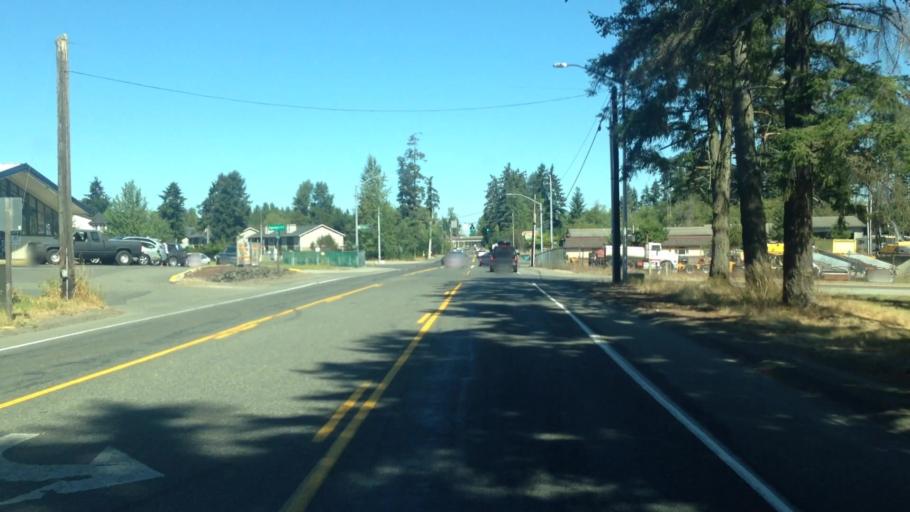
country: US
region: Washington
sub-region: Pierce County
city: Midland
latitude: 47.1539
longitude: -122.4155
